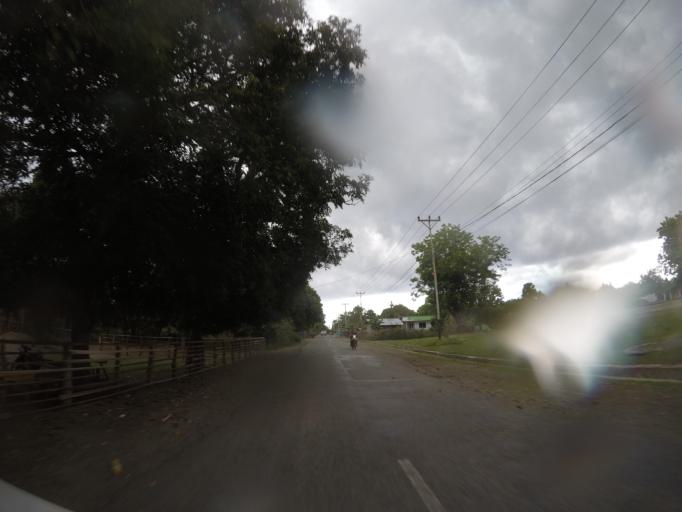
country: ID
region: East Nusa Tenggara
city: Atambua
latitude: -8.9498
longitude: 124.9753
